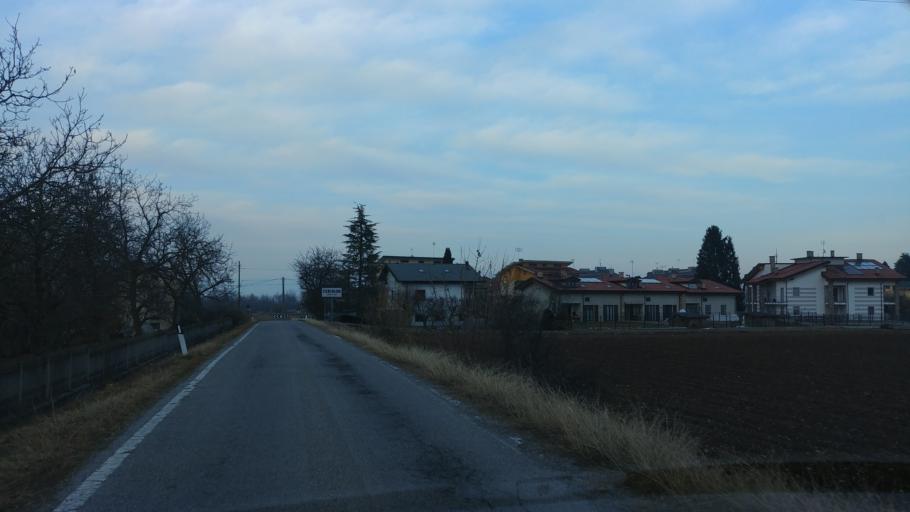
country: IT
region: Piedmont
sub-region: Provincia di Cuneo
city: Cuneo
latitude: 44.3983
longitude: 7.5278
